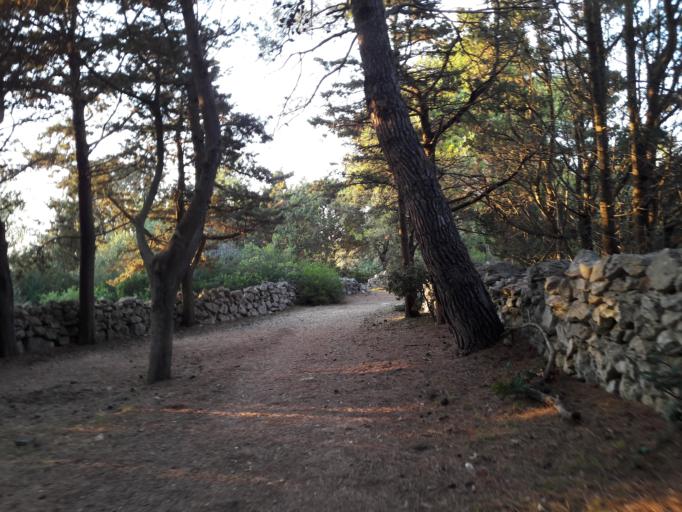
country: HR
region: Licko-Senjska
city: Novalja
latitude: 44.3682
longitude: 14.6967
